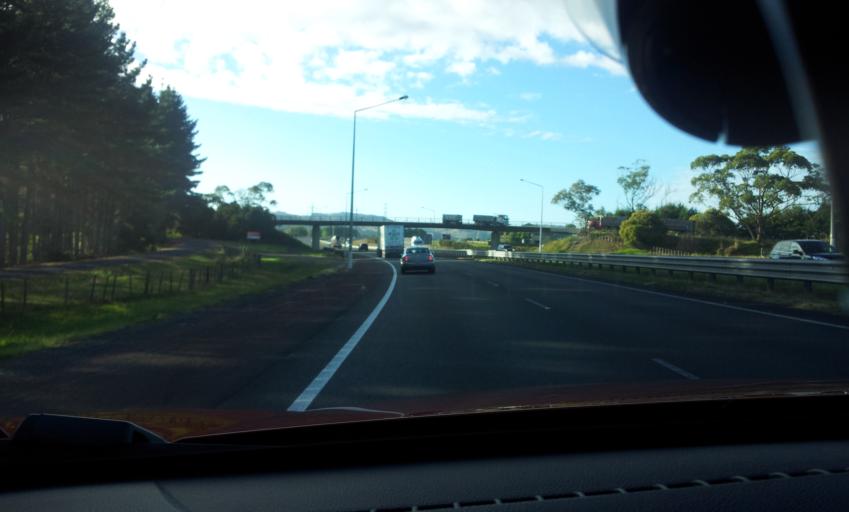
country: NZ
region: Auckland
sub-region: Auckland
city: Papakura
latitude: -37.1165
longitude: 174.9501
